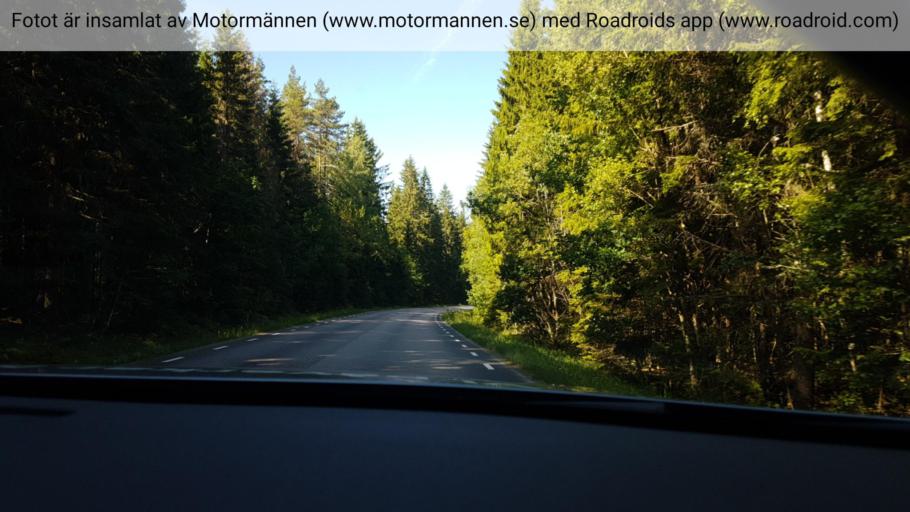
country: SE
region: Vaestra Goetaland
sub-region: Ulricehamns Kommun
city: Ulricehamn
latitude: 57.8311
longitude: 13.3115
